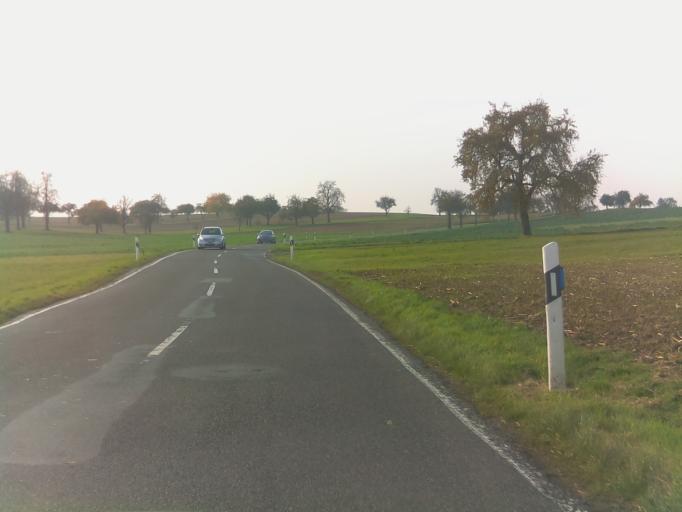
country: DE
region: Baden-Wuerttemberg
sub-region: Karlsruhe Region
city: Rosenberg
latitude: 49.3984
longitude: 9.5249
